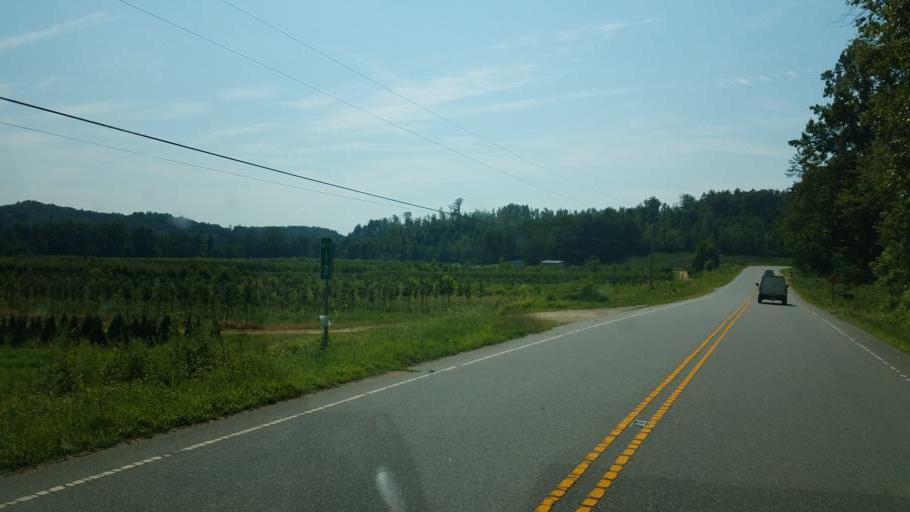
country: US
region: North Carolina
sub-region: Burke County
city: Glen Alpine
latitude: 35.8563
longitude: -81.7829
